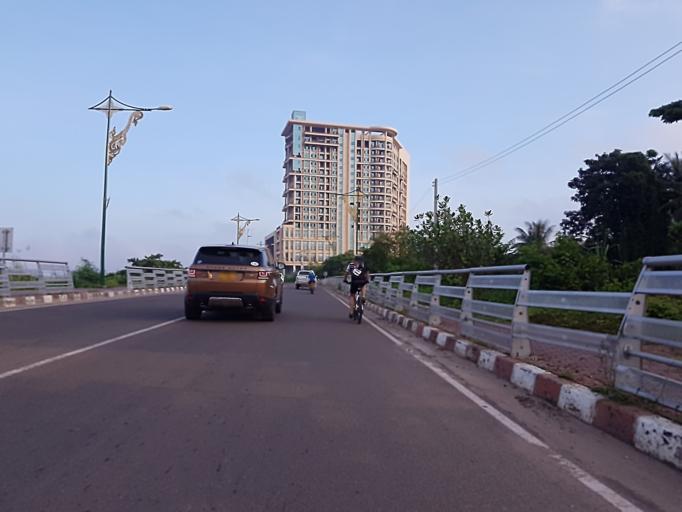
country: LA
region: Vientiane
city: Vientiane
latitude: 17.9398
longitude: 102.6174
